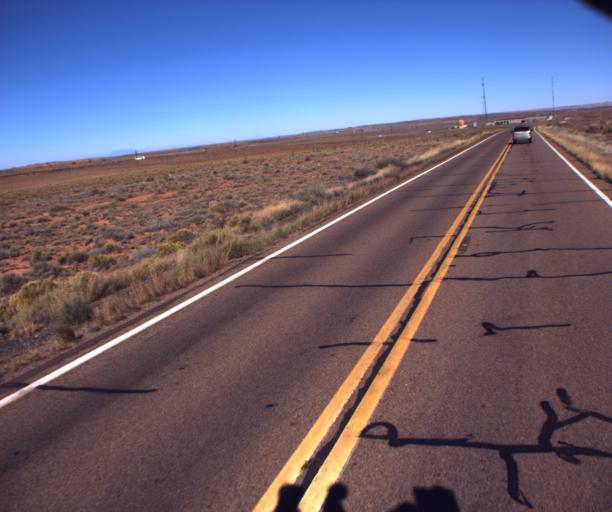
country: US
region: Arizona
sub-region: Navajo County
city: Holbrook
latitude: 34.8622
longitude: -110.1560
